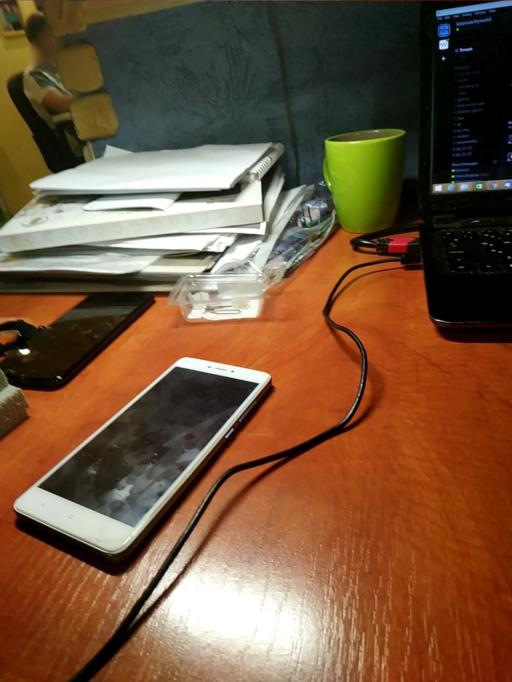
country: RU
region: Kaluga
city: Iznoski
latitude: 54.9552
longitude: 35.4308
